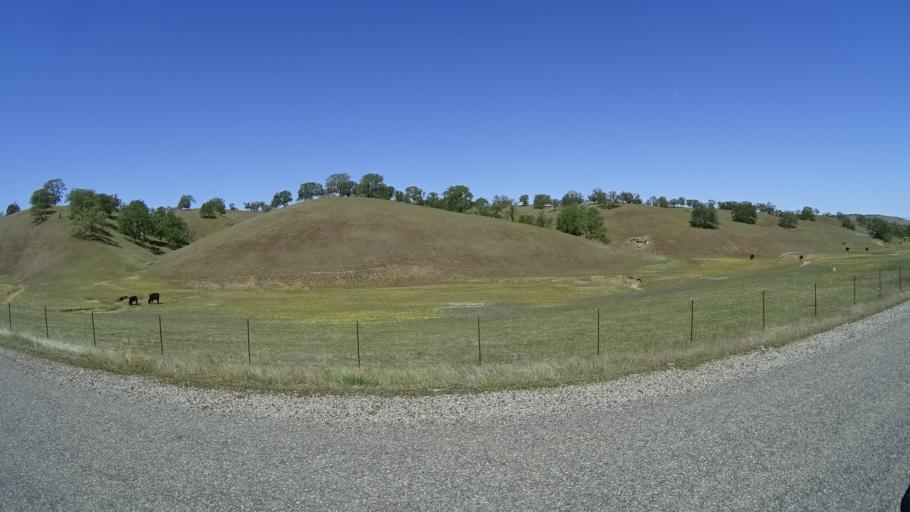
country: US
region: California
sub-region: Glenn County
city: Orland
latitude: 39.7446
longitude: -122.3727
